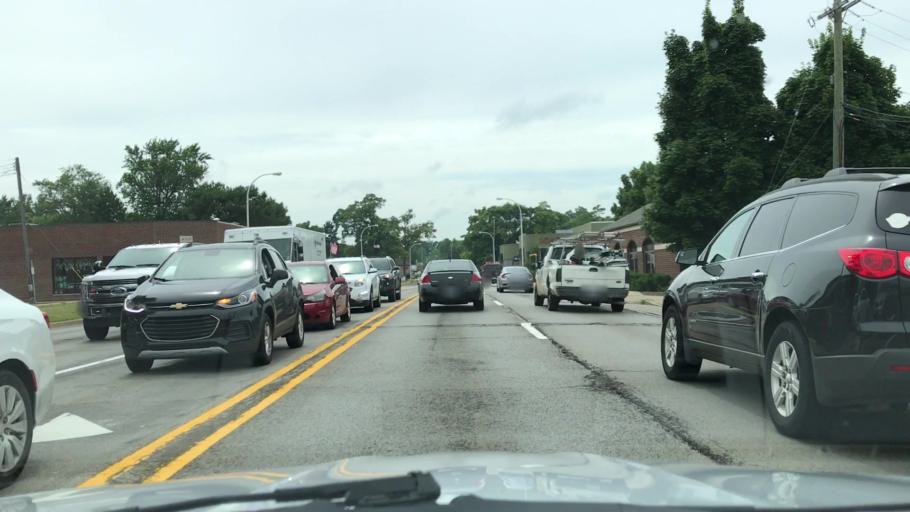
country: US
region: Michigan
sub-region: Oakland County
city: Keego Harbor
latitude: 42.6057
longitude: -83.3443
